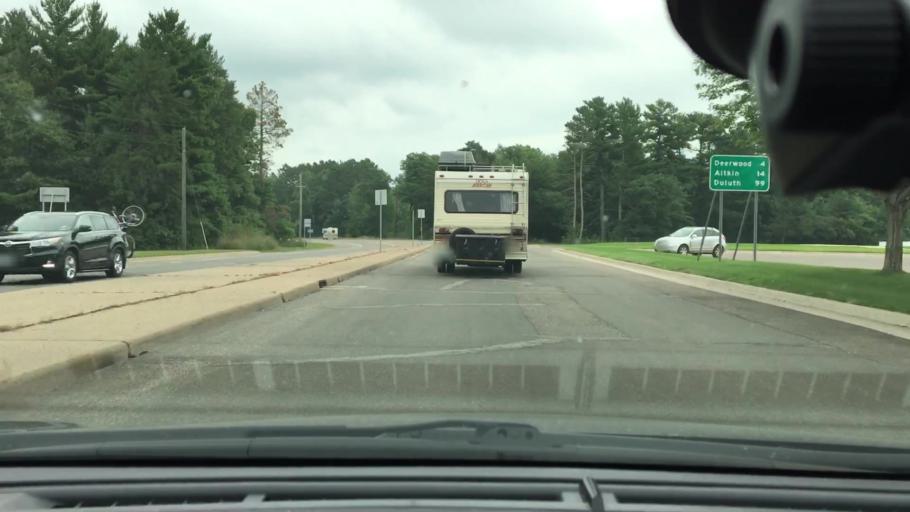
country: US
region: Minnesota
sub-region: Crow Wing County
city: Crosby
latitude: 46.4824
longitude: -93.9443
